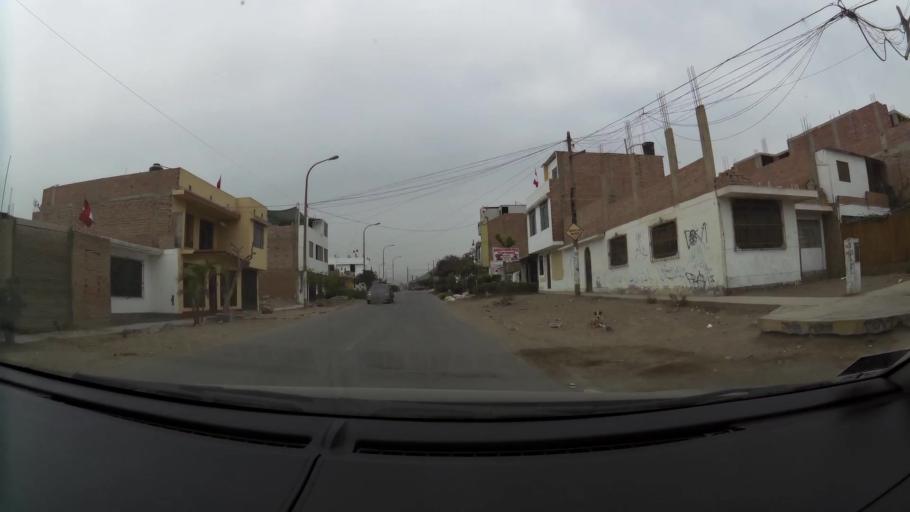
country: PE
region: Lima
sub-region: Lima
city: Santa Rosa
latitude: -11.7889
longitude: -77.1548
